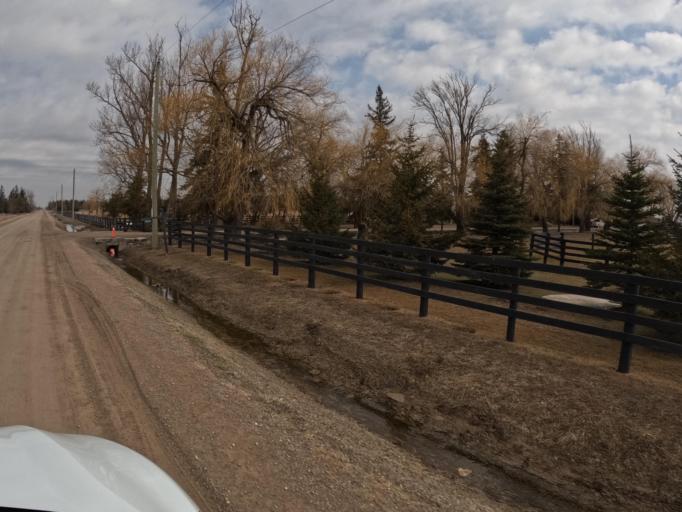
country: CA
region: Ontario
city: Orangeville
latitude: 43.9083
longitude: -80.2150
